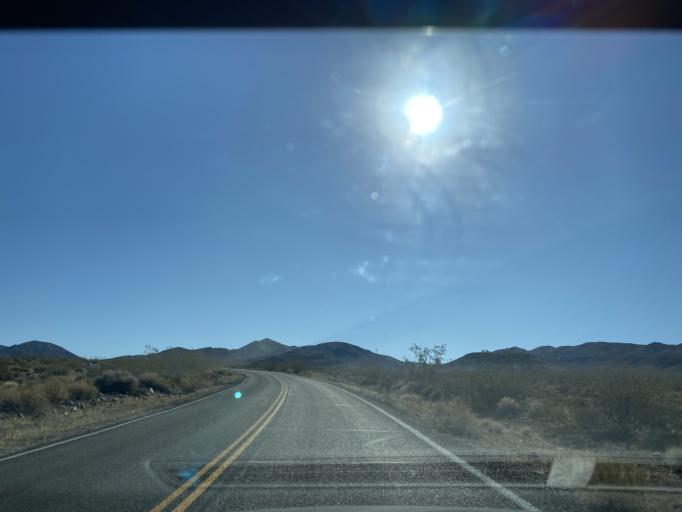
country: US
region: Nevada
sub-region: Nye County
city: Beatty
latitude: 36.2480
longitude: -116.6826
